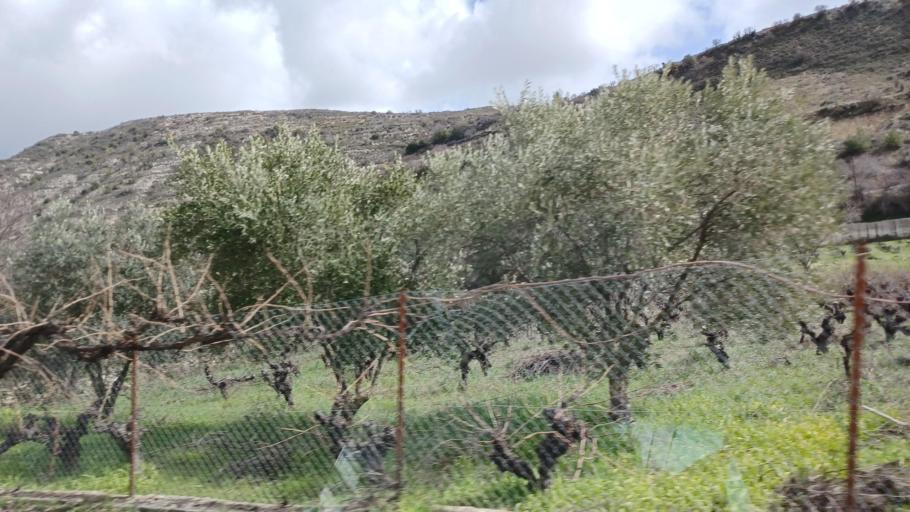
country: CY
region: Limassol
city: Pachna
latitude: 34.8453
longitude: 32.7429
